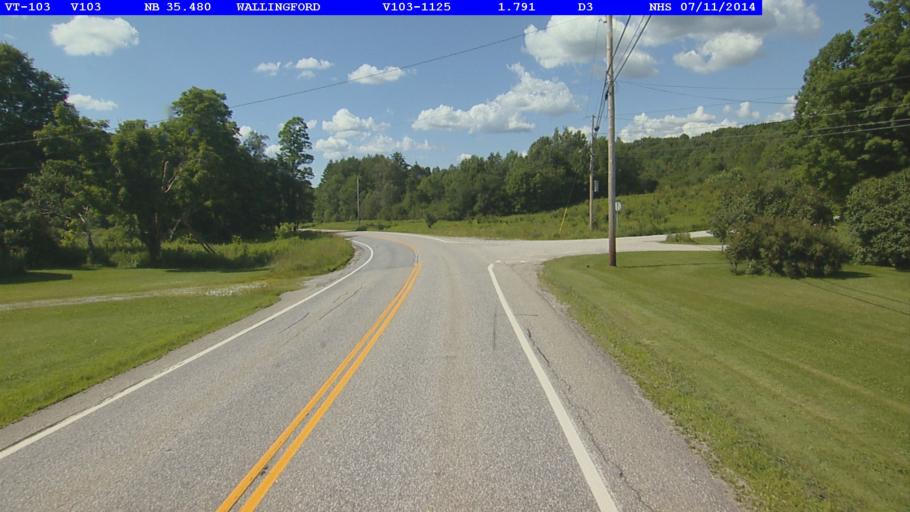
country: US
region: Vermont
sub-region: Rutland County
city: Rutland
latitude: 43.4756
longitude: -72.8754
